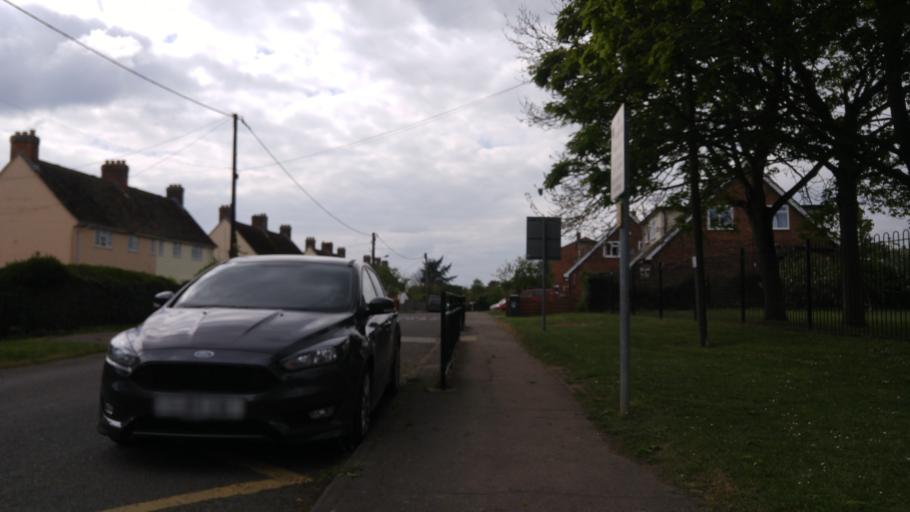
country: GB
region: England
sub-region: Essex
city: Earls Colne
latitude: 51.9427
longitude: 0.6944
